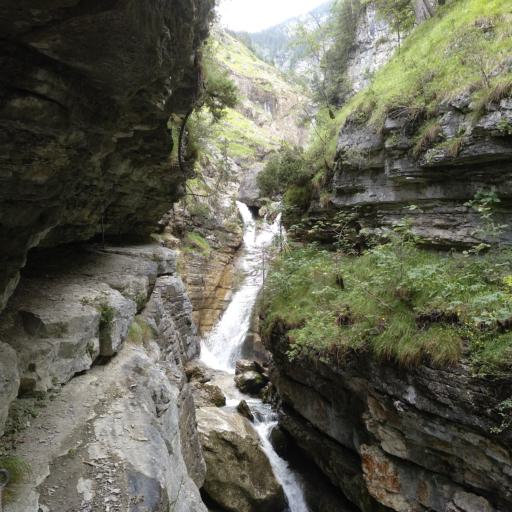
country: DE
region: Bavaria
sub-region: Upper Bavaria
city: Farchant
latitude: 47.5259
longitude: 11.1325
